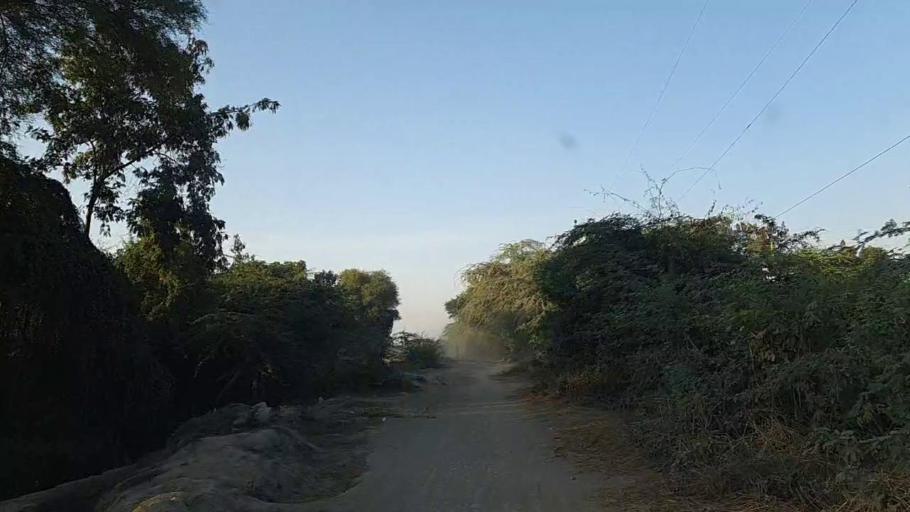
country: PK
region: Sindh
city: Mirpur Batoro
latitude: 24.7067
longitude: 68.2159
